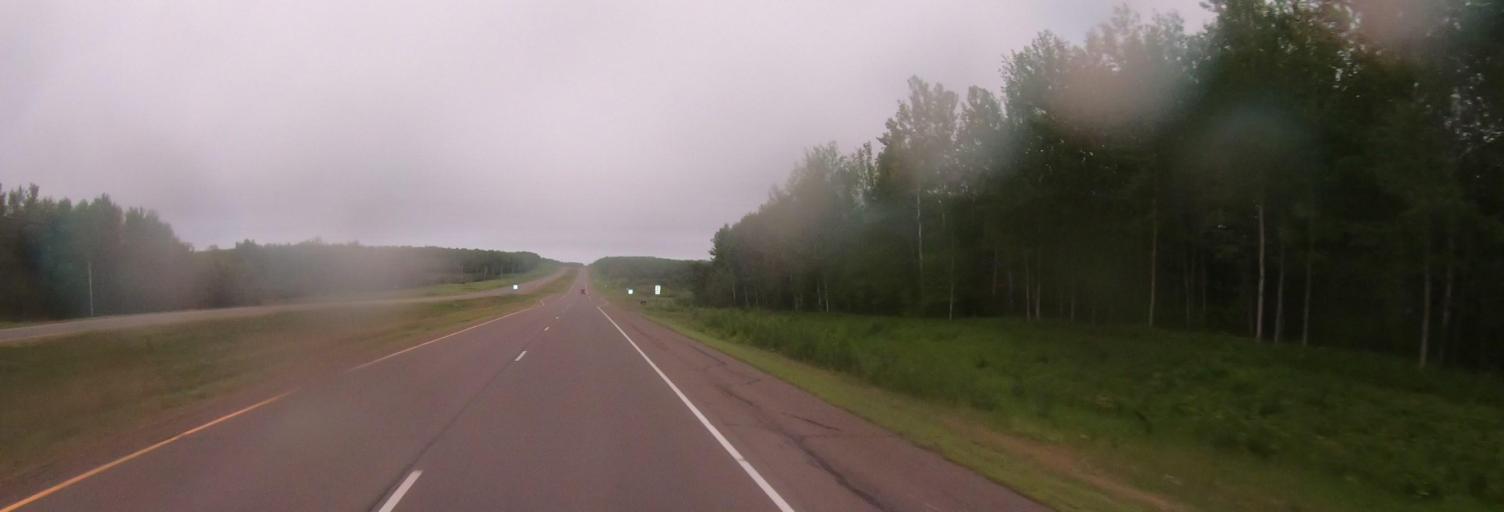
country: US
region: Minnesota
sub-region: Carlton County
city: Cloquet
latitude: 46.9215
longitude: -92.4701
